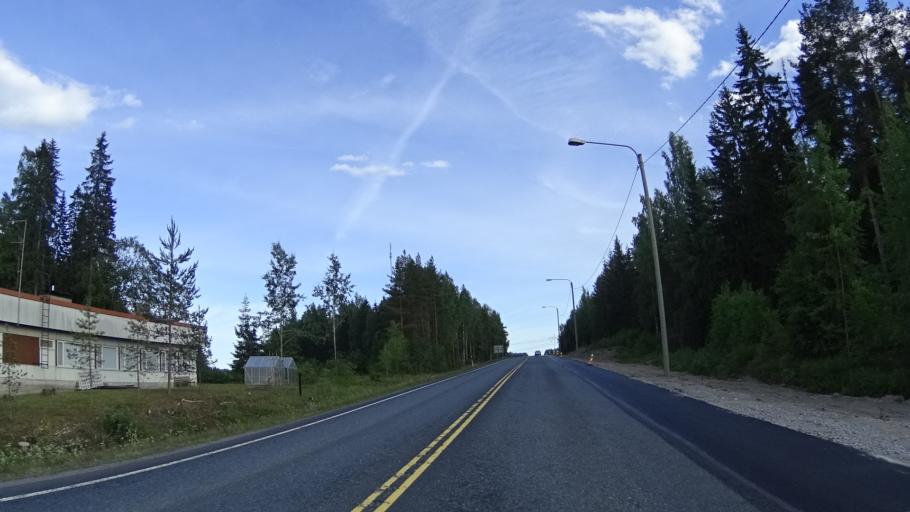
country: FI
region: Haeme
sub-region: Forssa
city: Forssa
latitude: 60.7792
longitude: 23.6683
